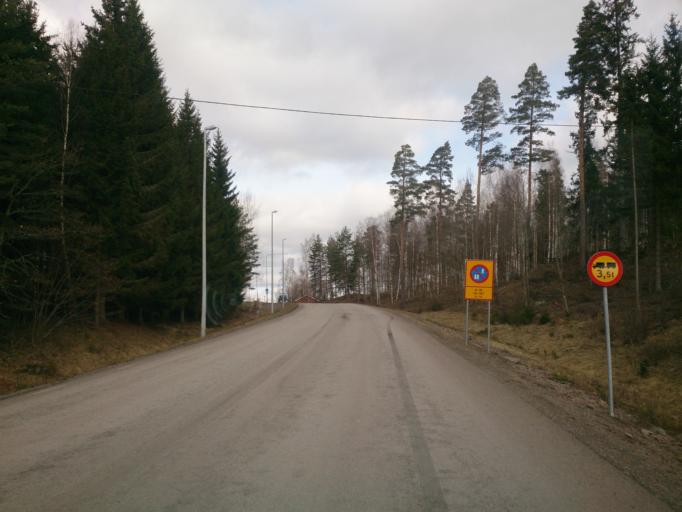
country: SE
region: OEstergoetland
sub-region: Atvidabergs Kommun
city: Atvidaberg
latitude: 58.1831
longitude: 16.0140
